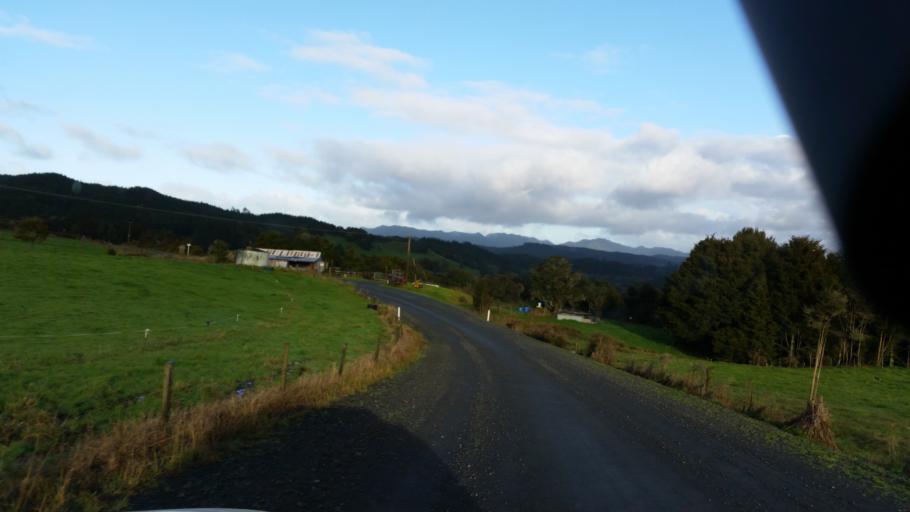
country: NZ
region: Northland
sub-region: Whangarei
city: Maungatapere
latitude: -35.7594
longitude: 174.0775
